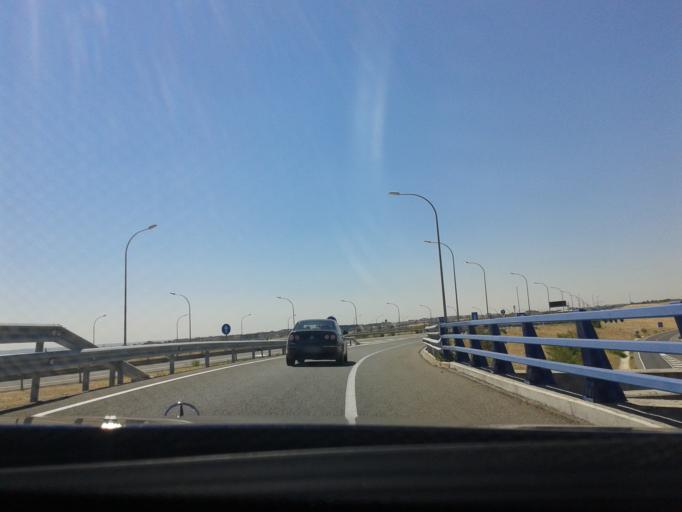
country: ES
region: Madrid
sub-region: Provincia de Madrid
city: Barajas de Madrid
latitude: 40.4929
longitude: -3.6029
